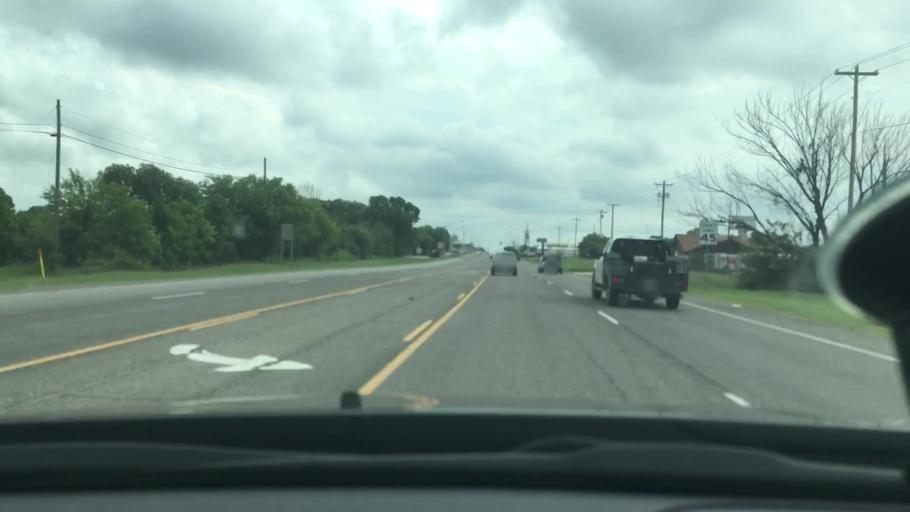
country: US
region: Oklahoma
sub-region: Carter County
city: Lone Grove
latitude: 34.1731
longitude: -97.2692
